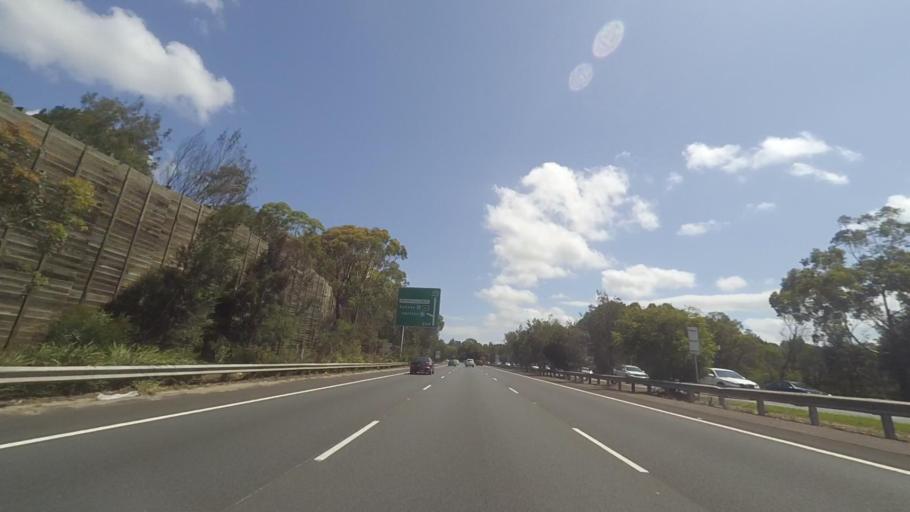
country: AU
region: New South Wales
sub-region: Ku-ring-gai
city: North Wahroonga
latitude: -33.6973
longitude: 151.1199
